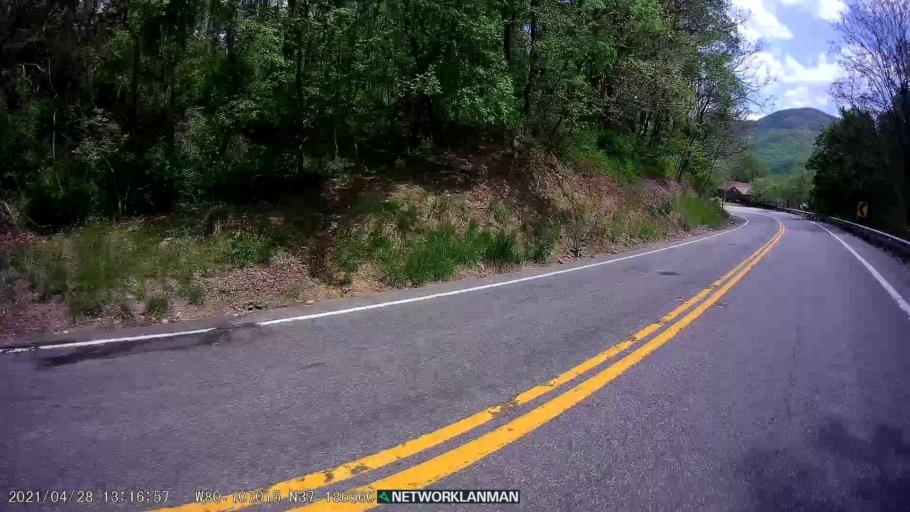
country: US
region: Virginia
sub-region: Roanoke County
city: Cave Spring
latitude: 37.1864
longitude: -80.1067
